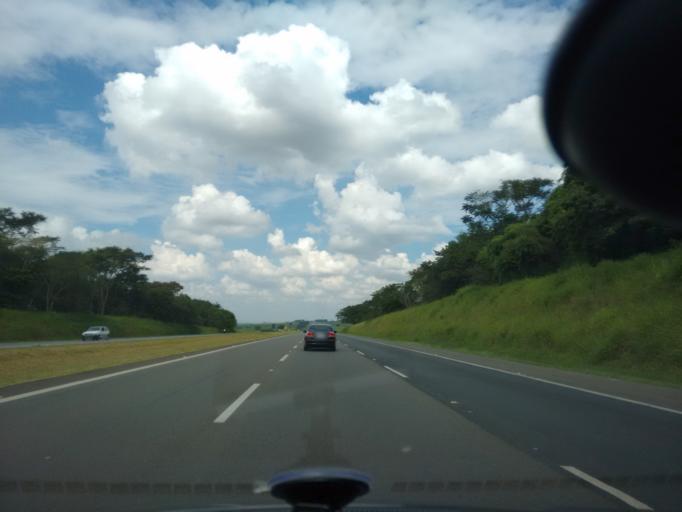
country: BR
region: Sao Paulo
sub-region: Nova Odessa
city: Nova Odessa
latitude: -22.8299
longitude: -47.3640
